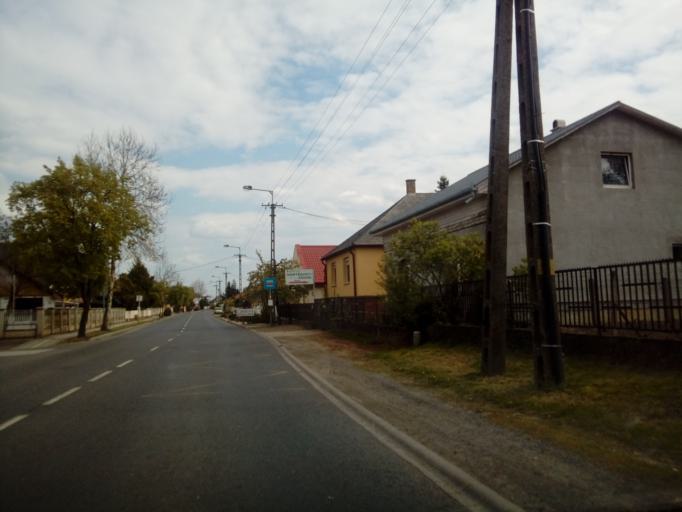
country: HU
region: Szabolcs-Szatmar-Bereg
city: Nagykallo
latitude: 47.8786
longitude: 21.8324
